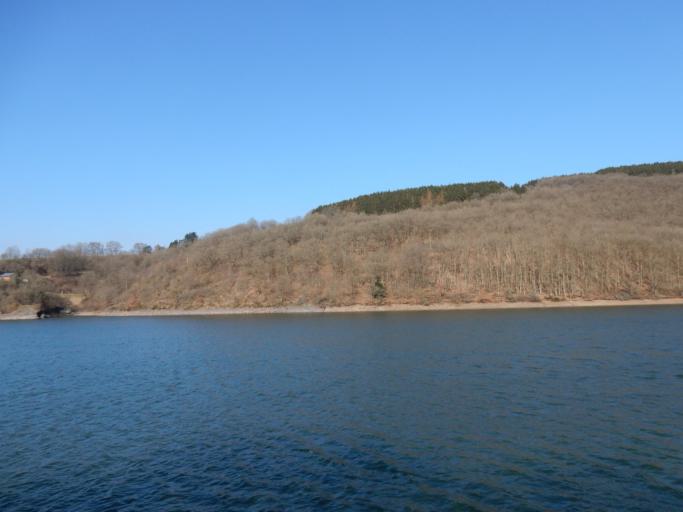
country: LU
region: Diekirch
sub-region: Canton de Wiltz
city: Bavigne
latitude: 49.9048
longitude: 5.8841
